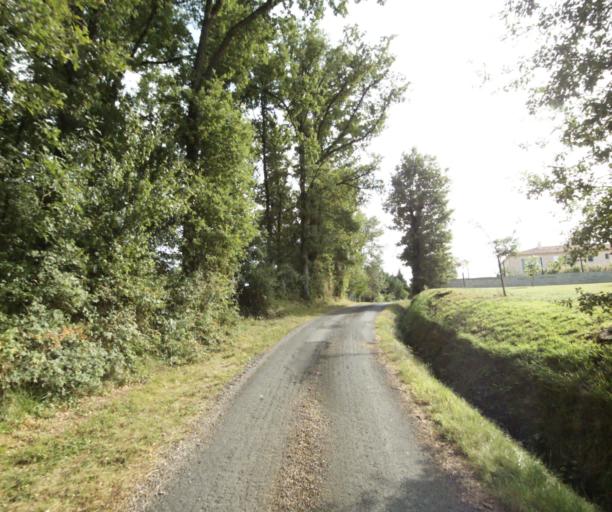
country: FR
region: Midi-Pyrenees
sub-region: Departement du Tarn
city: Soual
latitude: 43.5430
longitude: 2.0643
